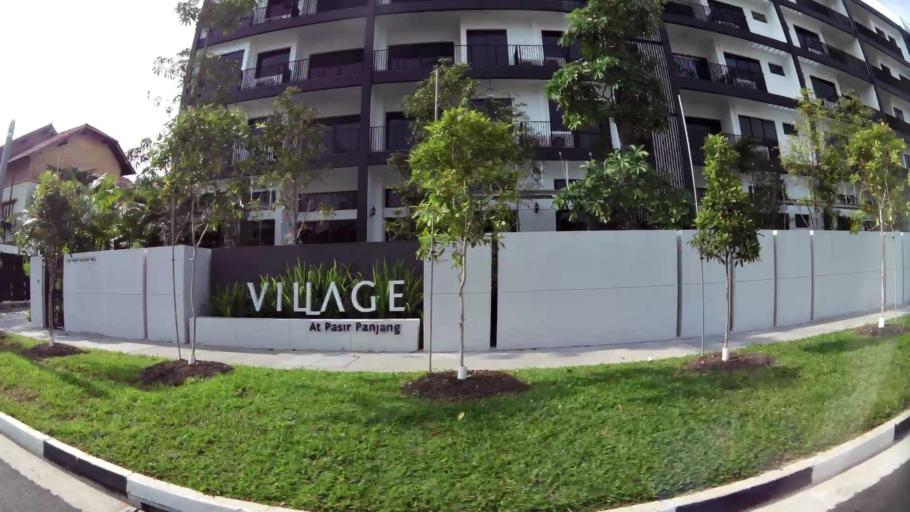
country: SG
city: Singapore
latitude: 1.2914
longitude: 103.7706
